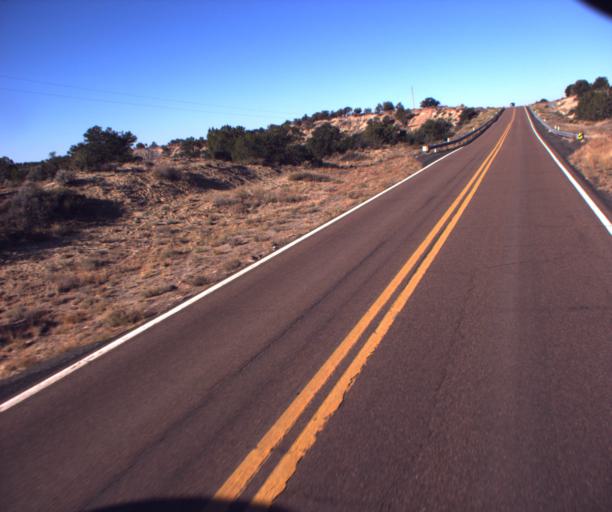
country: US
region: Arizona
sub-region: Apache County
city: Ganado
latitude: 35.7482
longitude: -109.9184
